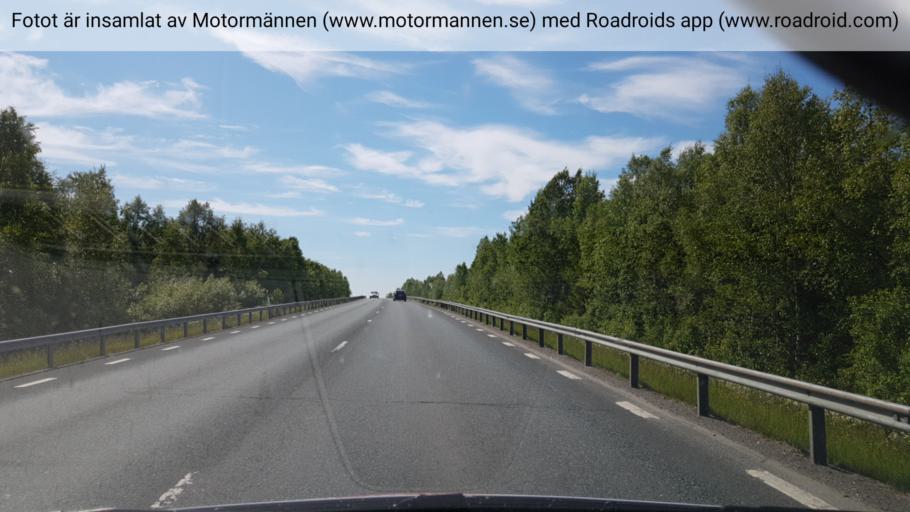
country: SE
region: Norrbotten
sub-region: Haparanda Kommun
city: Haparanda
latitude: 65.8368
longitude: 24.1019
